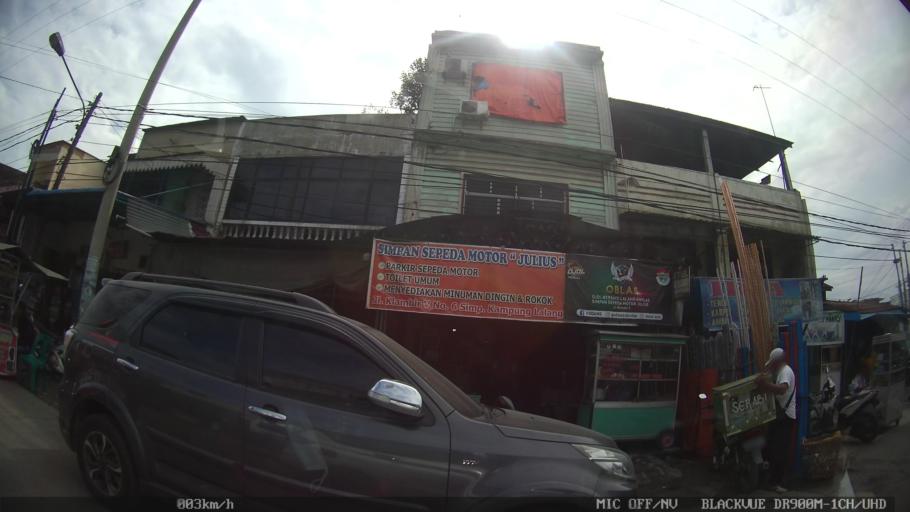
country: ID
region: North Sumatra
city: Sunggal
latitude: 3.5984
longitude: 98.6090
